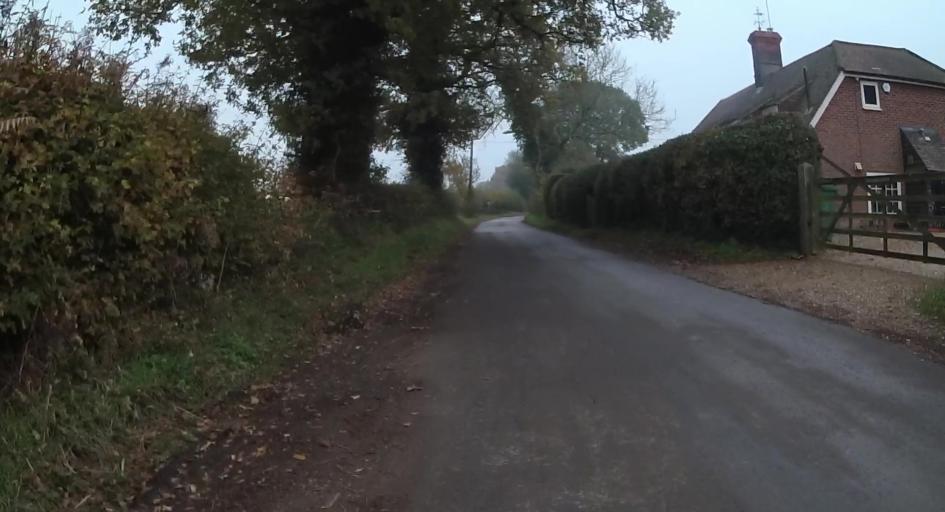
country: GB
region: England
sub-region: Hampshire
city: Old Basing
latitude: 51.1980
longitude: -1.0372
